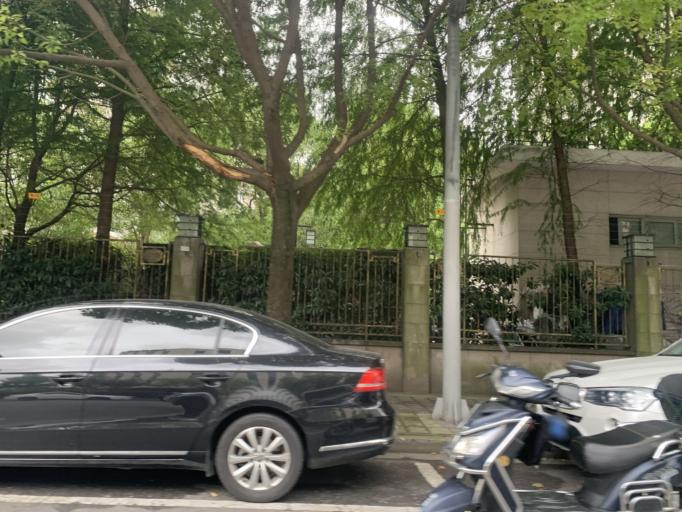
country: CN
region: Shanghai Shi
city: Huamu
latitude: 31.2090
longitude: 121.5542
